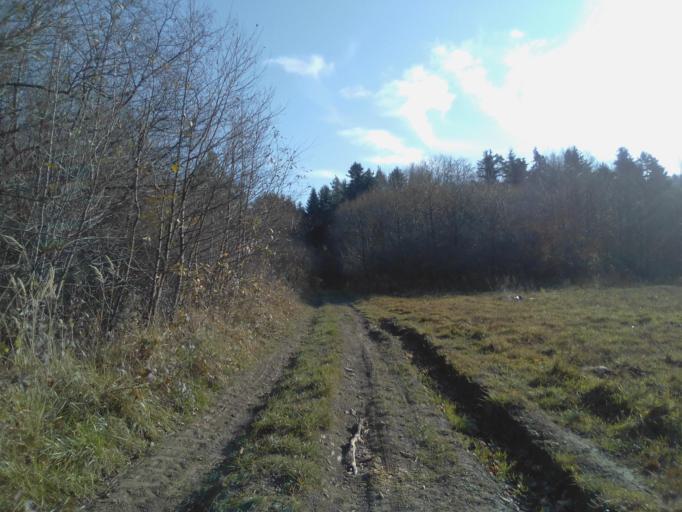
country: PL
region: Subcarpathian Voivodeship
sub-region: Powiat strzyzowski
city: Jawornik
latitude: 49.7930
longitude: 21.8832
